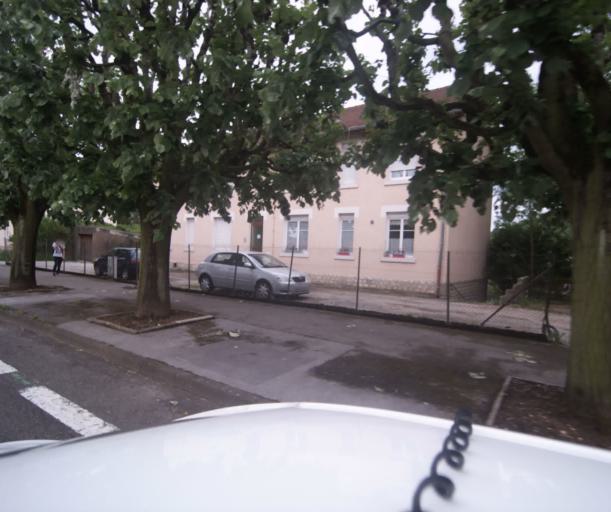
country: FR
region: Franche-Comte
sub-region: Departement du Doubs
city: Besancon
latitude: 47.2320
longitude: 5.9998
